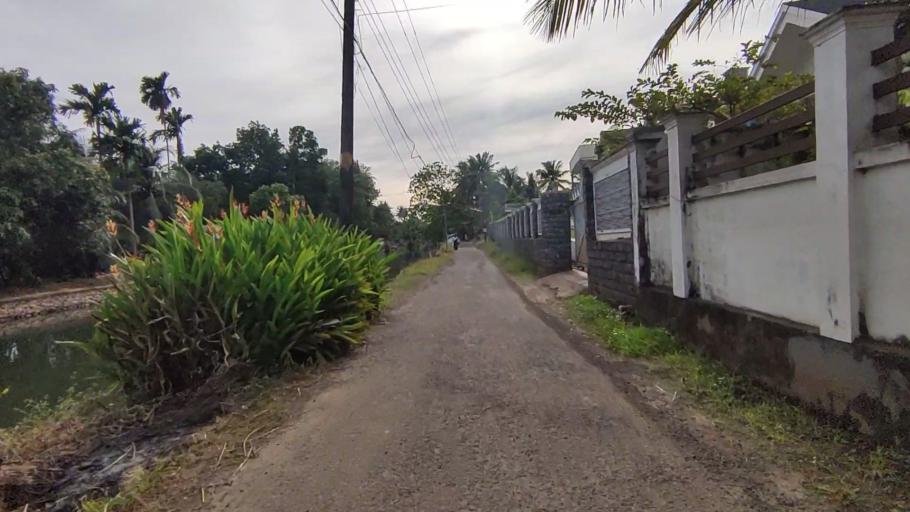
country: IN
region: Kerala
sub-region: Kottayam
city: Kottayam
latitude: 9.5700
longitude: 76.4919
